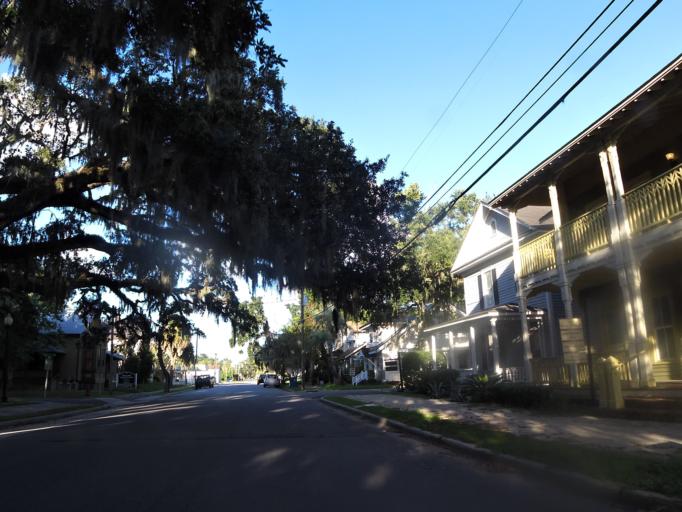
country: US
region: Georgia
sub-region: Glynn County
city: Brunswick
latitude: 31.1524
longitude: -81.4941
